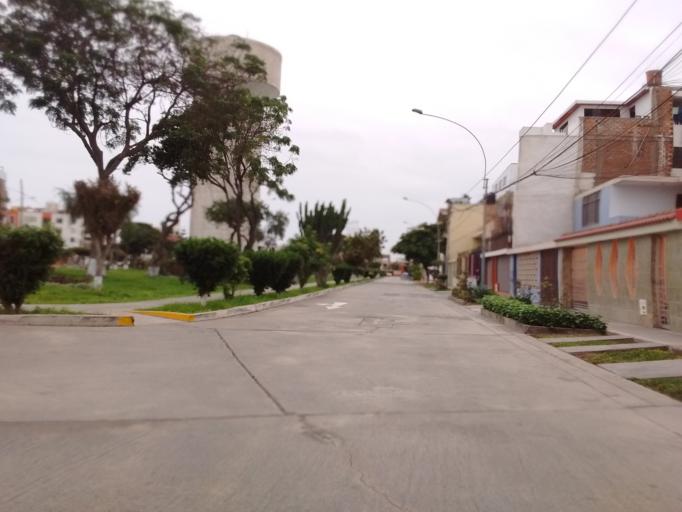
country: PE
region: Callao
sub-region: Callao
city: Callao
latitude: -12.0665
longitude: -77.0947
